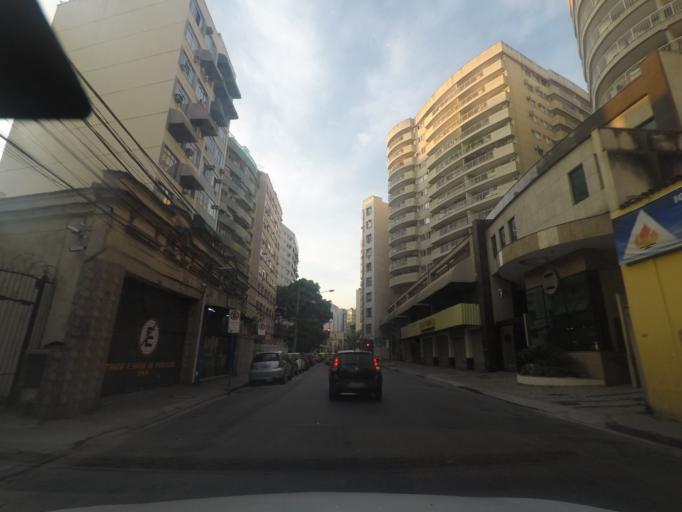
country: BR
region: Rio de Janeiro
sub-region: Rio De Janeiro
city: Rio de Janeiro
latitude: -22.9275
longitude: -43.1793
